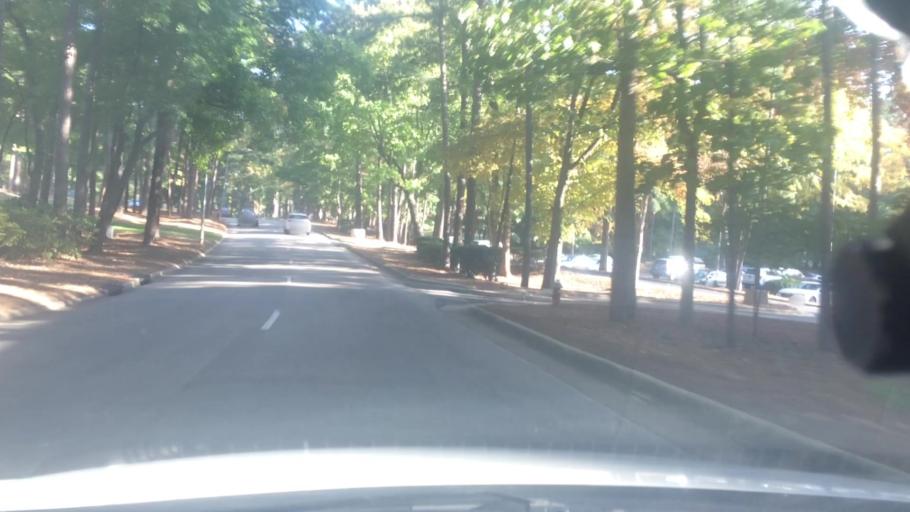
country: US
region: North Carolina
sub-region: Wake County
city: Raleigh
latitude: 35.8205
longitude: -78.6053
